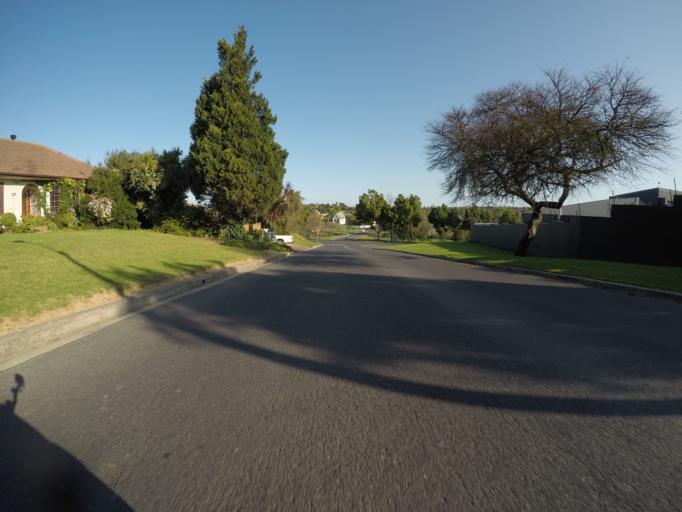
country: ZA
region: Western Cape
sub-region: City of Cape Town
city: Kraaifontein
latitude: -33.8463
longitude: 18.6593
